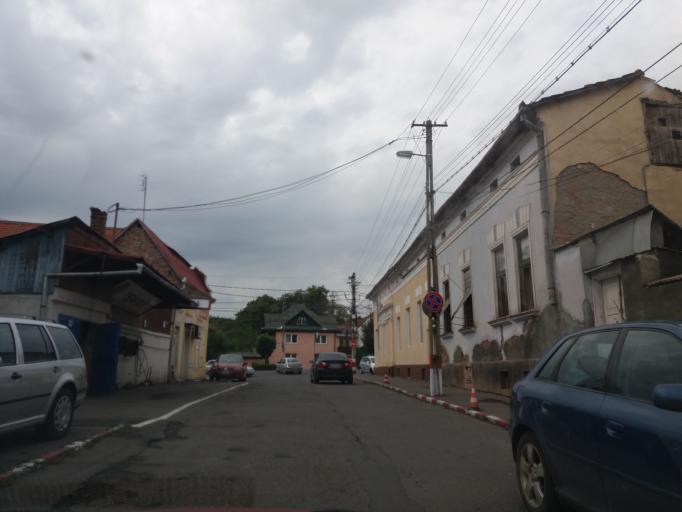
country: RO
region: Mures
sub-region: Municipiul Reghin
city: Reghin
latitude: 46.7770
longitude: 24.6992
